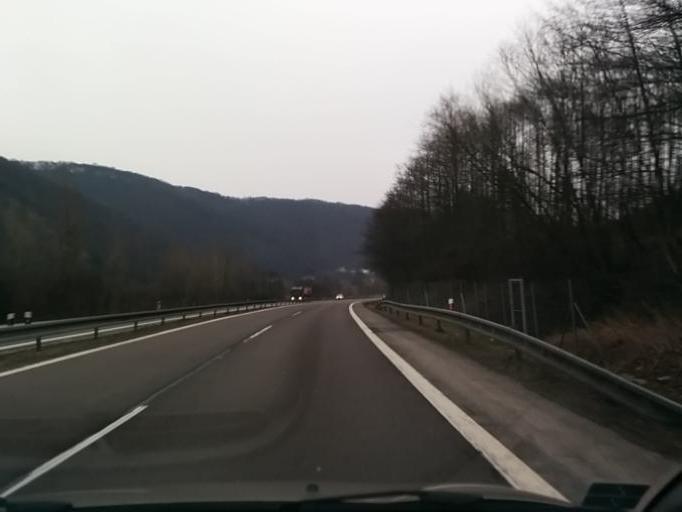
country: SK
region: Banskobystricky
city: Ziar nad Hronom
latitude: 48.5821
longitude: 18.9732
